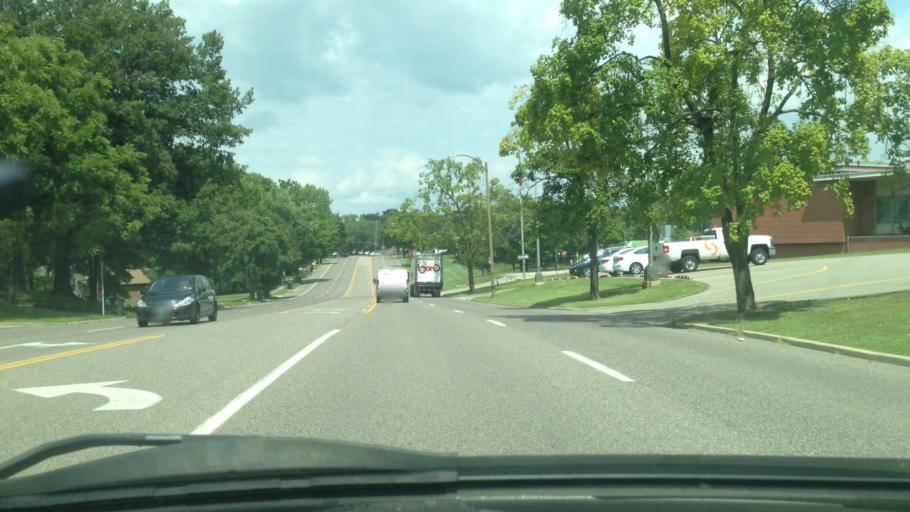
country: US
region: Missouri
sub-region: Saint Louis County
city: Shrewsbury
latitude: 38.5967
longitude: -90.3261
